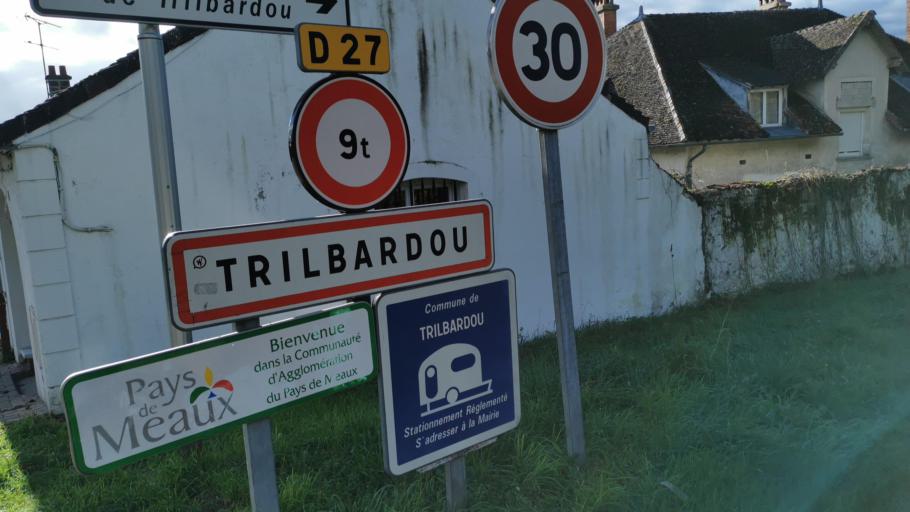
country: FR
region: Ile-de-France
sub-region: Departement de Seine-et-Marne
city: Esbly
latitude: 48.9433
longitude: 2.8071
